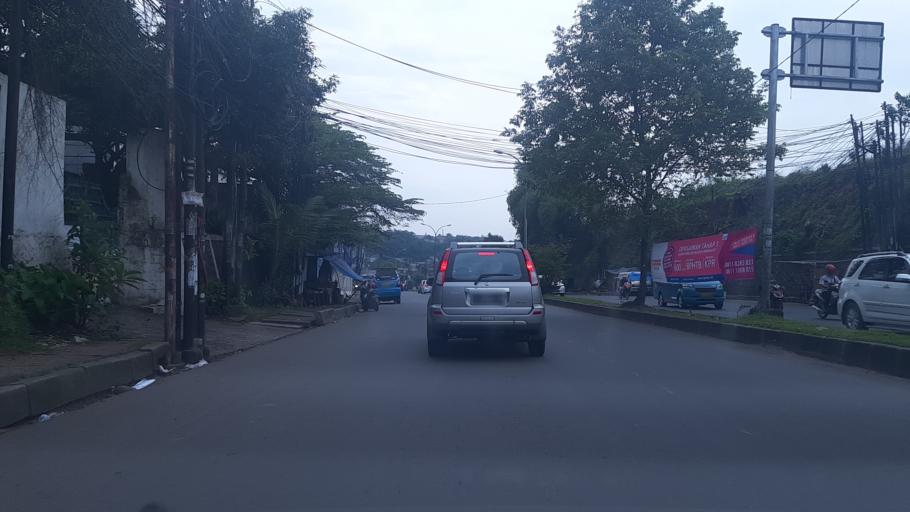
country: ID
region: West Java
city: Citeureup
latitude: -6.4820
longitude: 106.8697
